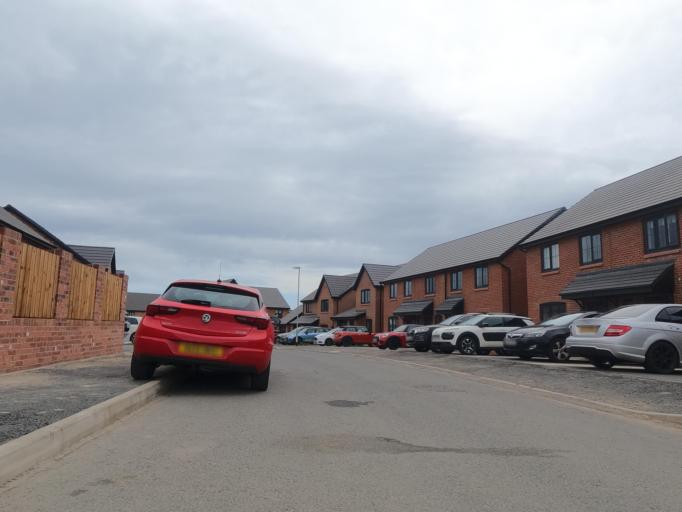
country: GB
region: England
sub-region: Northumberland
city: Blyth
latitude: 55.1113
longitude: -1.5396
